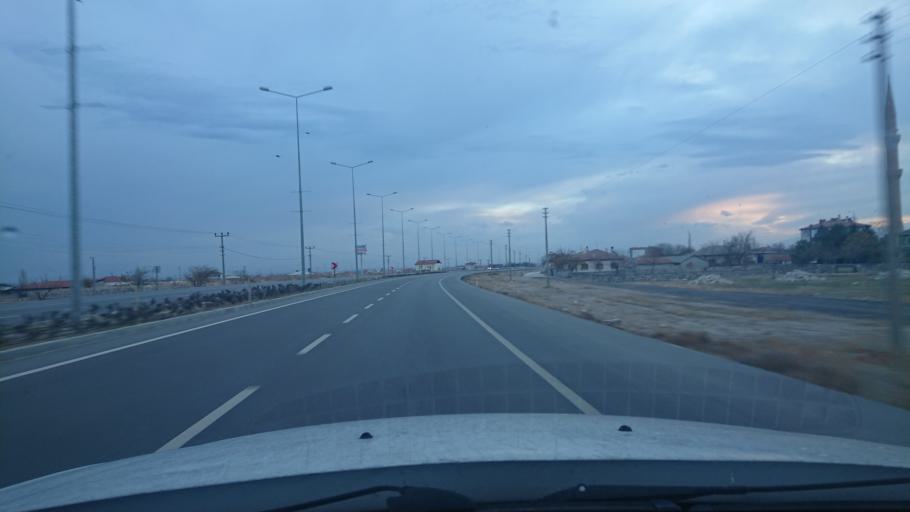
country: TR
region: Aksaray
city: Sultanhani
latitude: 38.2529
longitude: 33.5532
